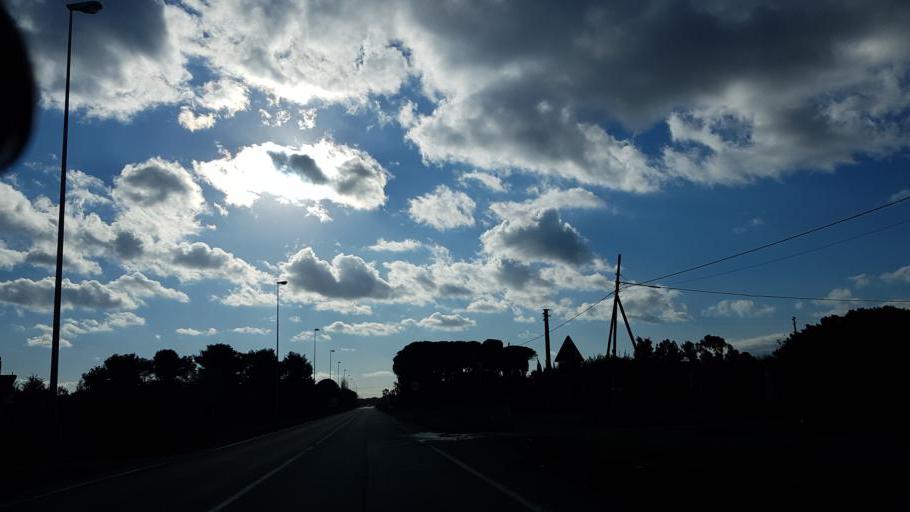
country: IT
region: Apulia
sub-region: Provincia di Brindisi
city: Brindisi
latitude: 40.6564
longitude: 17.9296
